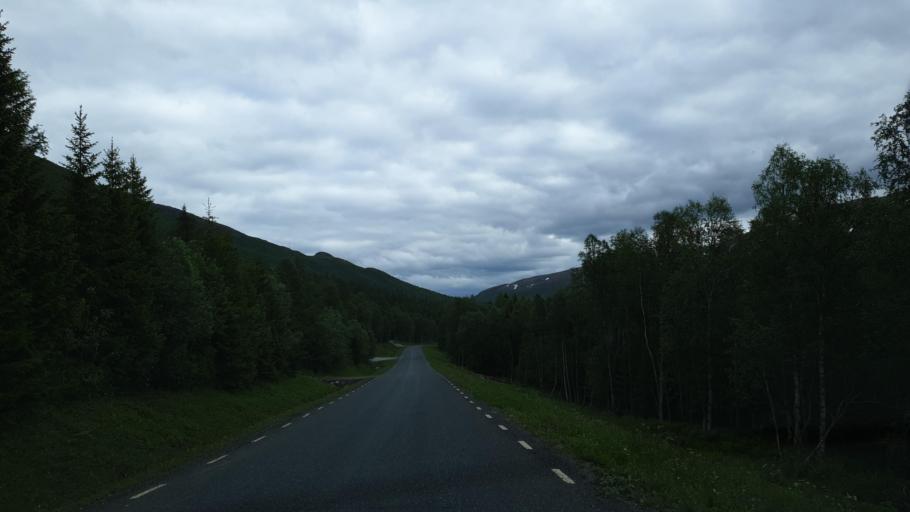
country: NO
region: Nordland
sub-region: Hattfjelldal
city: Hattfjelldal
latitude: 65.4394
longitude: 14.5628
